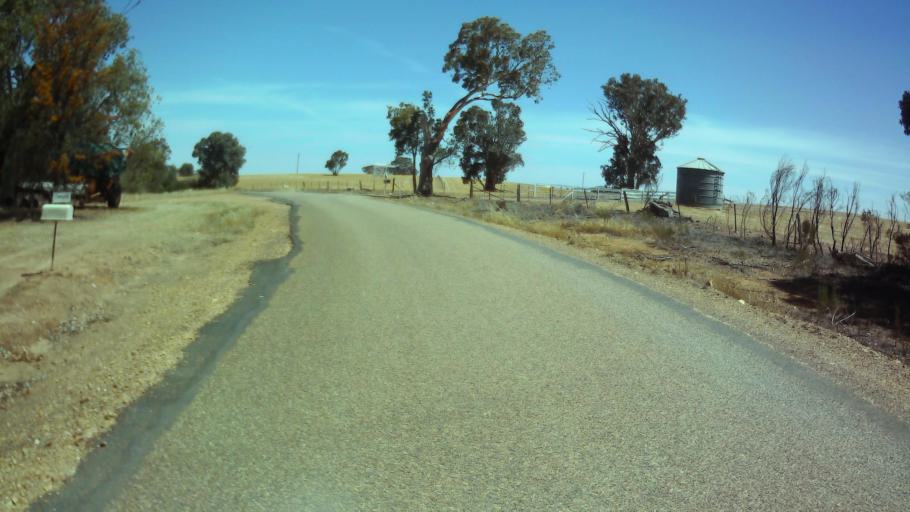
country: AU
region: New South Wales
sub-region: Weddin
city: Grenfell
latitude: -33.9097
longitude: 148.1776
